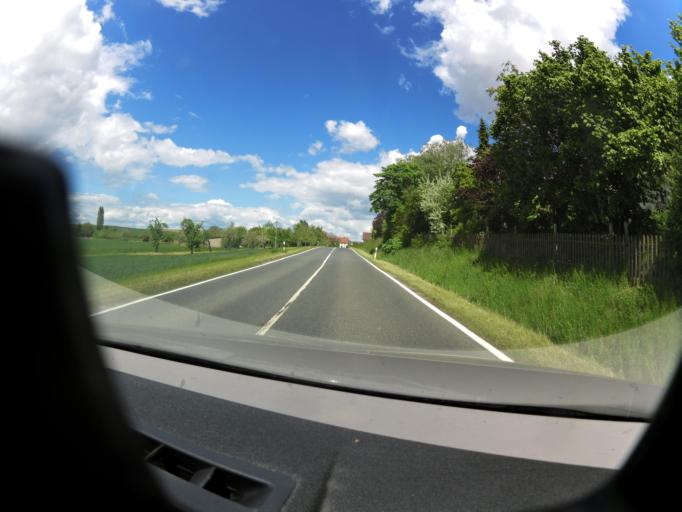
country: DE
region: Bavaria
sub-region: Regierungsbezirk Unterfranken
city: Prosselsheim
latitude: 49.8753
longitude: 10.1244
